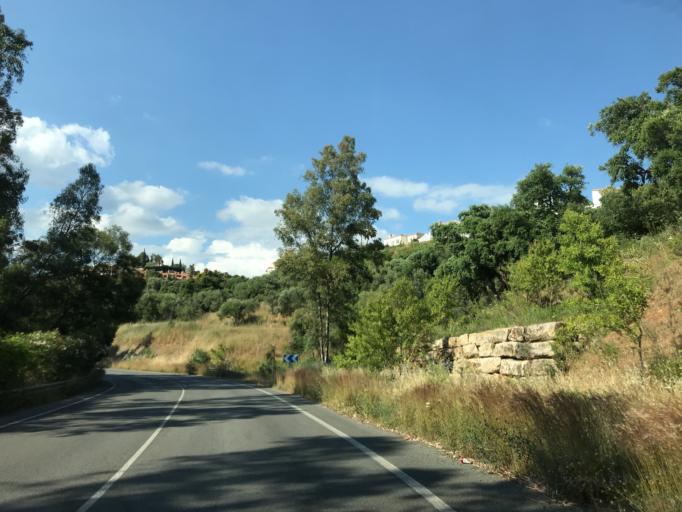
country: ES
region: Andalusia
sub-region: Provincia de Malaga
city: Benahavis
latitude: 36.5041
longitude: -5.0136
